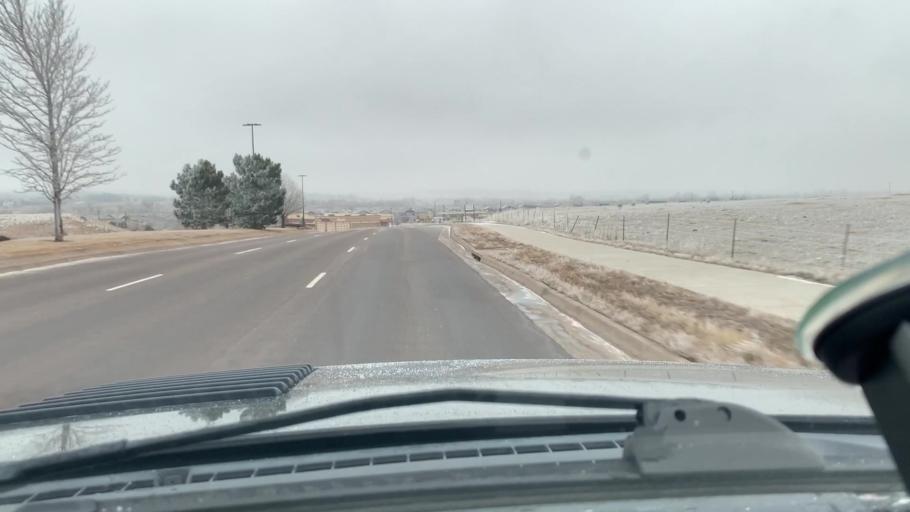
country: US
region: Colorado
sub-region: Arapahoe County
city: Dove Valley
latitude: 39.5760
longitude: -104.8116
